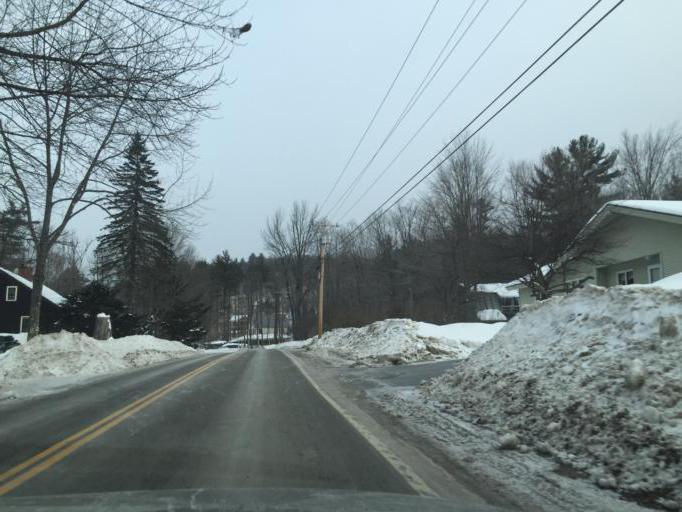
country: US
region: New Hampshire
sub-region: Carroll County
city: North Conway
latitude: 44.1034
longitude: -71.1502
